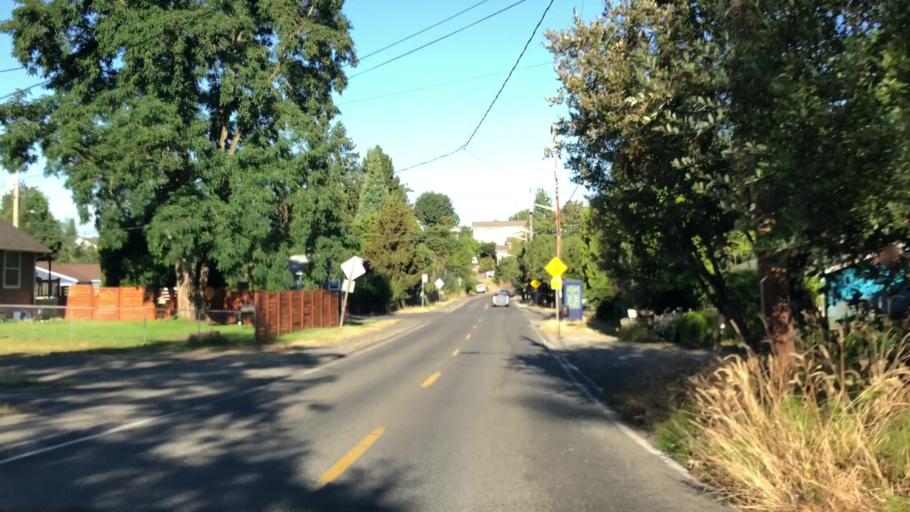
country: US
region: Washington
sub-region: King County
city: White Center
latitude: 47.5558
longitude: -122.3563
